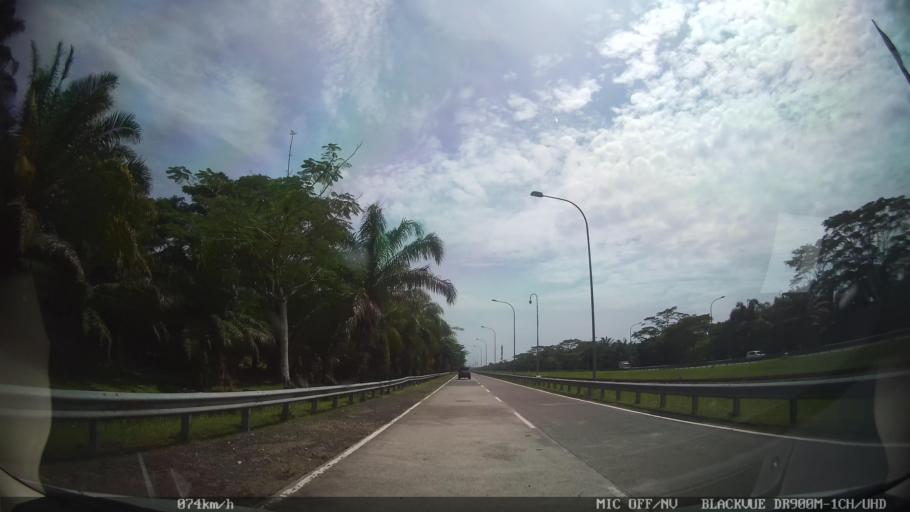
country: ID
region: North Sumatra
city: Percut
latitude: 3.6157
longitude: 98.8591
